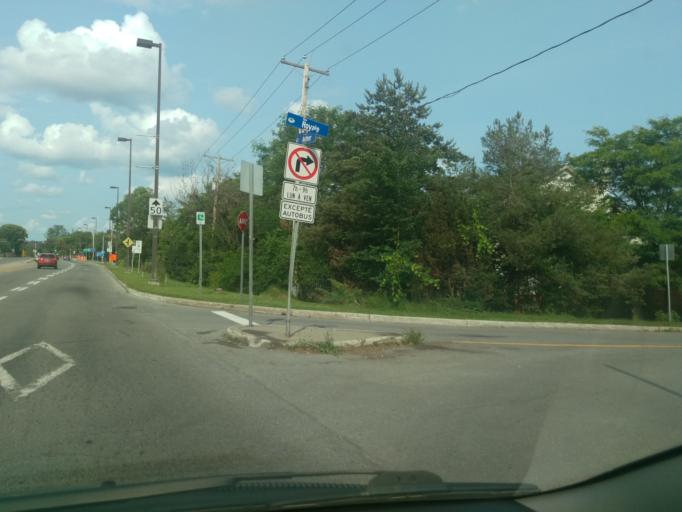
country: CA
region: Ontario
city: Ottawa
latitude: 45.4162
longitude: -75.7627
